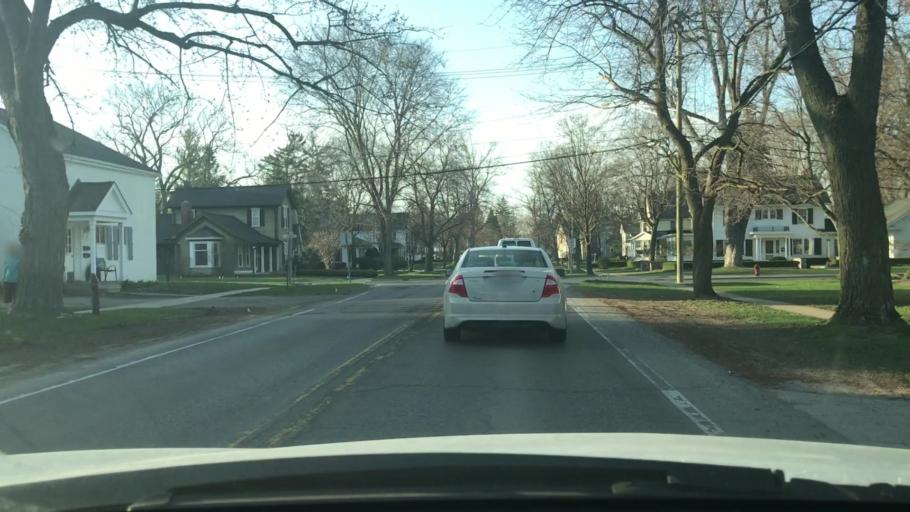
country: US
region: Michigan
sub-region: Oakland County
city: Clarkston
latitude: 42.7354
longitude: -83.4221
